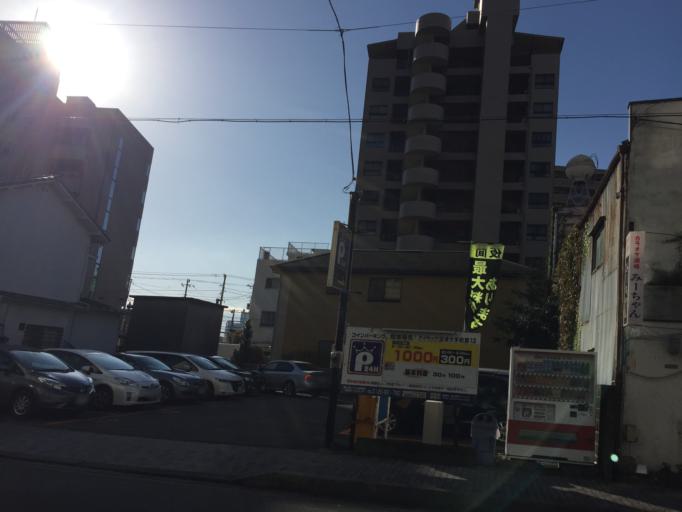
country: JP
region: Shizuoka
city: Numazu
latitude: 35.1002
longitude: 138.8621
